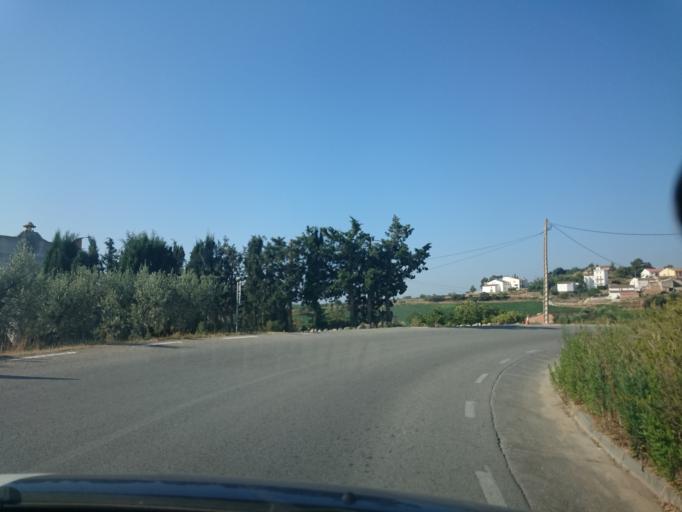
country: ES
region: Catalonia
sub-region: Provincia de Barcelona
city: Vilobi del Penedes
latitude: 41.4169
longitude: 1.6552
